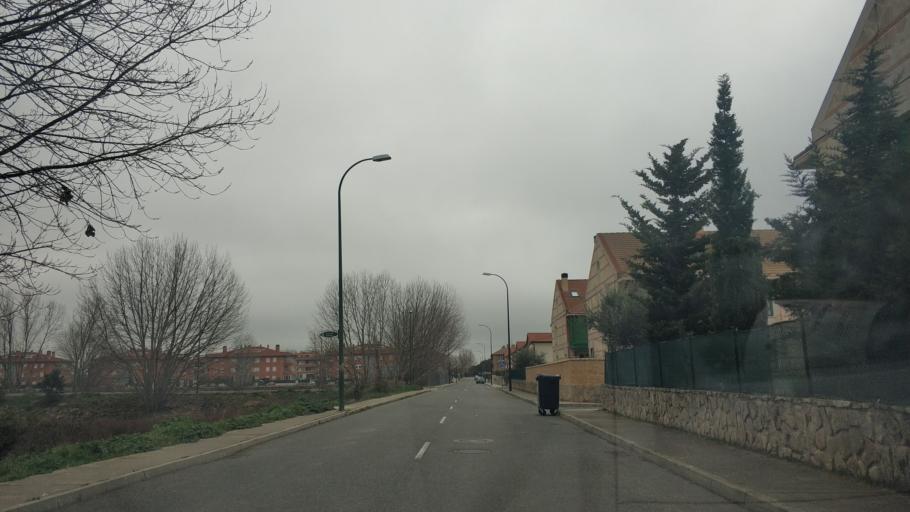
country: ES
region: Castille and Leon
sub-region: Provincia de Salamanca
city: Villamayor
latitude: 40.9964
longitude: -5.7254
